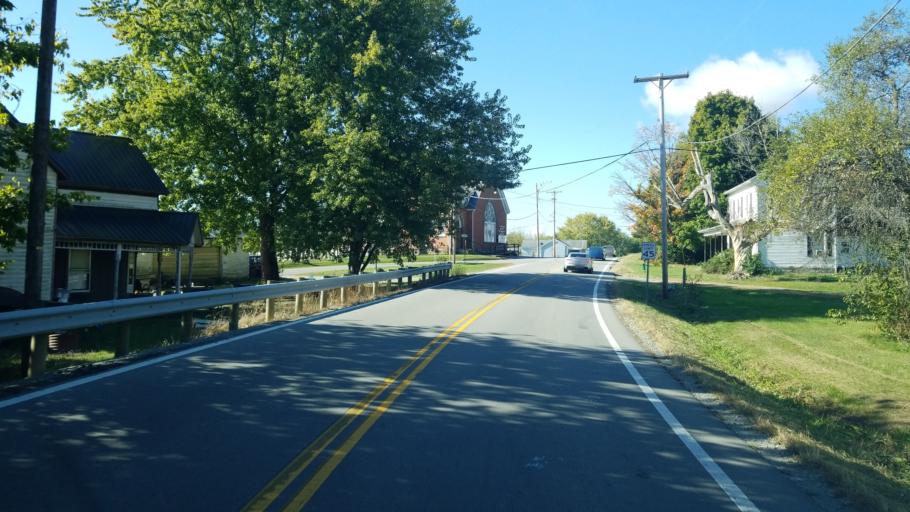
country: US
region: Ohio
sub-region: Fayette County
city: Washington Court House
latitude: 39.4766
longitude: -83.4803
